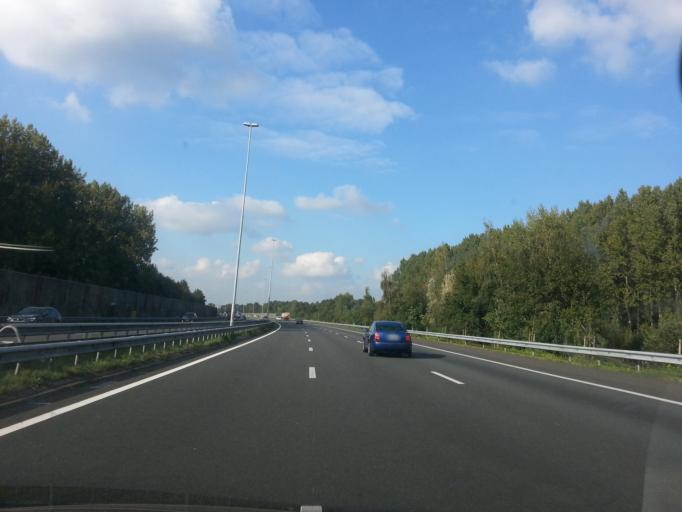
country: NL
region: North Brabant
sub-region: Gemeente Boxtel
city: Boxtel
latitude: 51.5858
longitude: 5.3542
